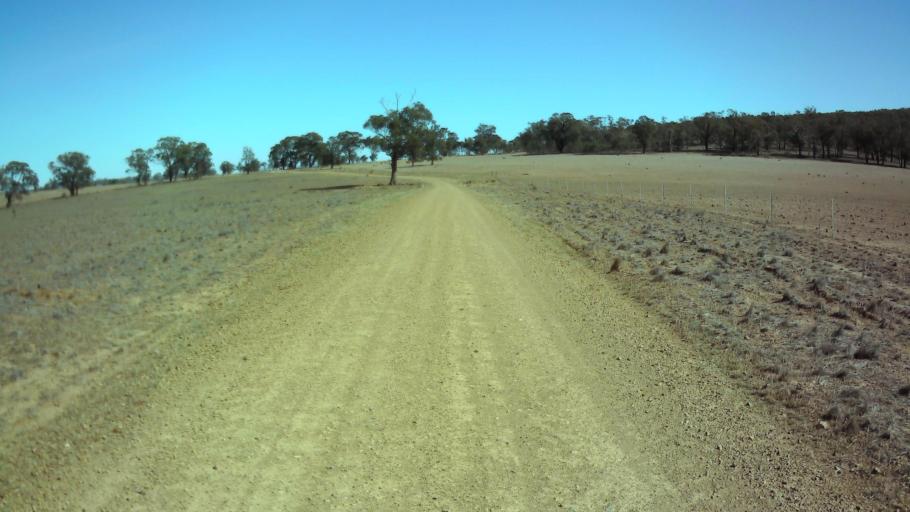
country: AU
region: New South Wales
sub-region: Weddin
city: Grenfell
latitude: -33.7610
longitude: 147.9222
